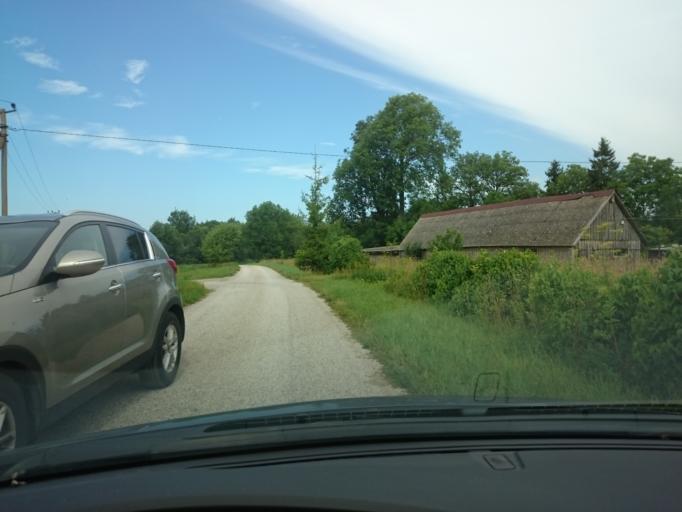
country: EE
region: Laeaene
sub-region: Ridala Parish
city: Uuemoisa
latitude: 58.9939
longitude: 23.6610
